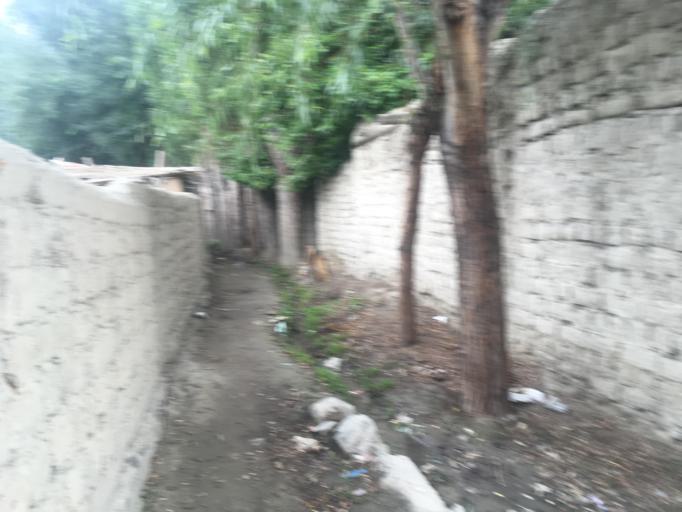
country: PK
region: Gilgit-Baltistan
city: Skardu
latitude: 35.2930
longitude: 75.6487
